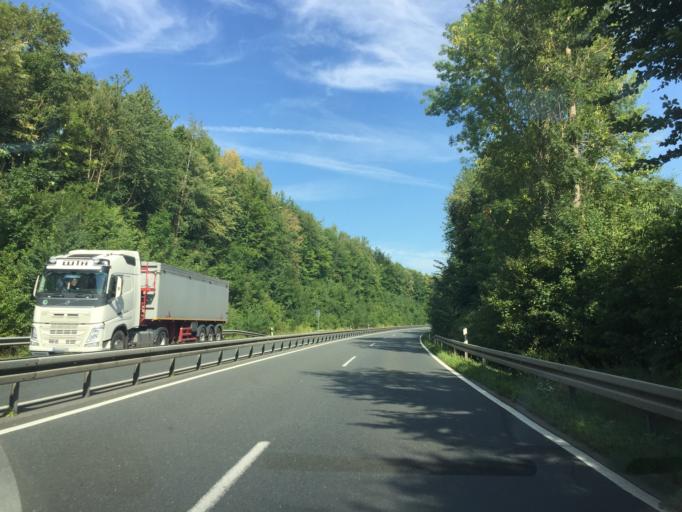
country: DE
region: Lower Saxony
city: Gittelde
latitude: 51.8019
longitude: 10.1917
